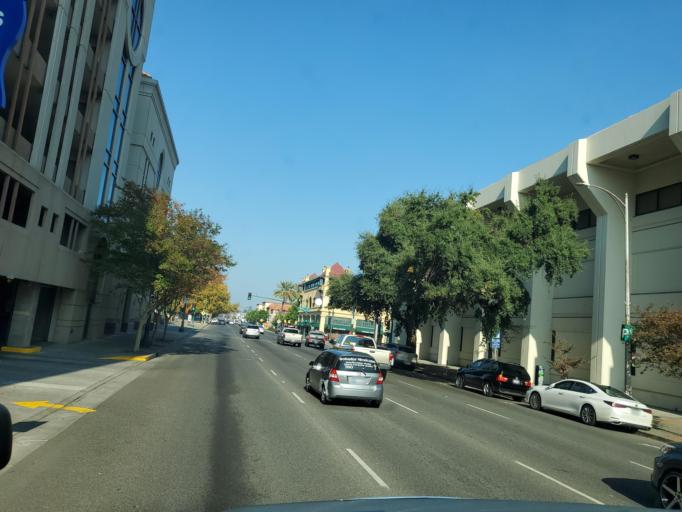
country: US
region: California
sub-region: San Joaquin County
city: Stockton
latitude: 37.9530
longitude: -121.2900
